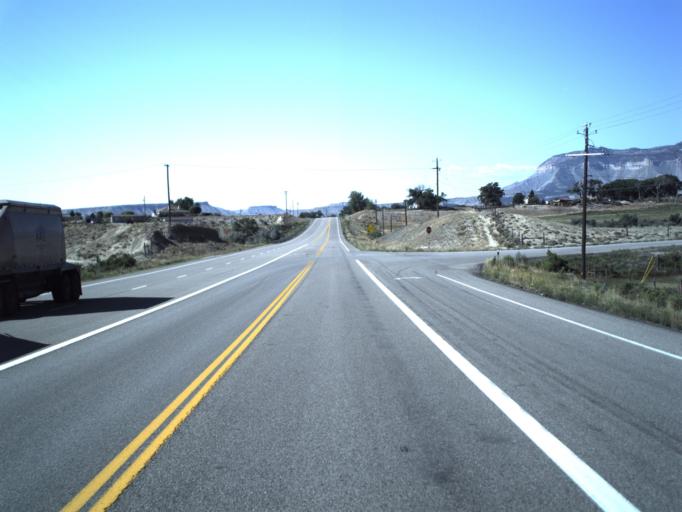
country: US
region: Utah
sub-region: Emery County
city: Ferron
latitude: 39.1057
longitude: -111.1289
